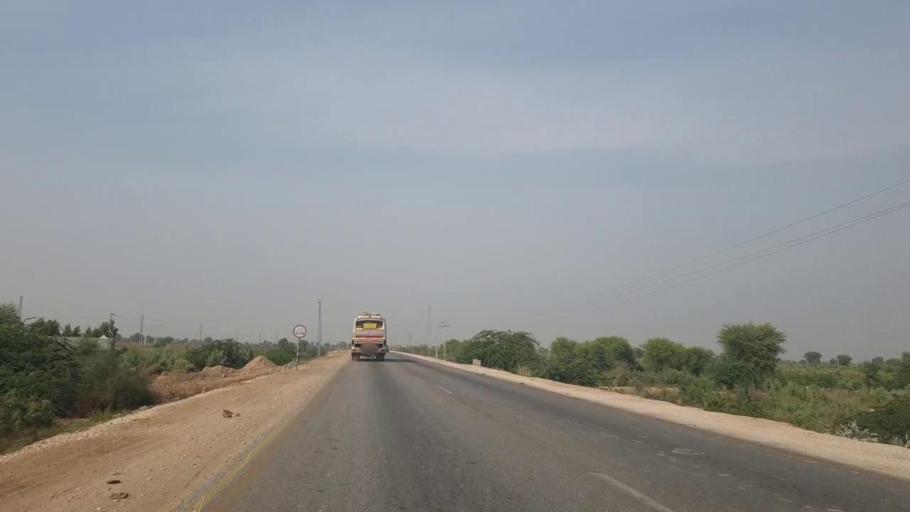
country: PK
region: Sindh
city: Sann
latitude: 26.0761
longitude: 68.0966
